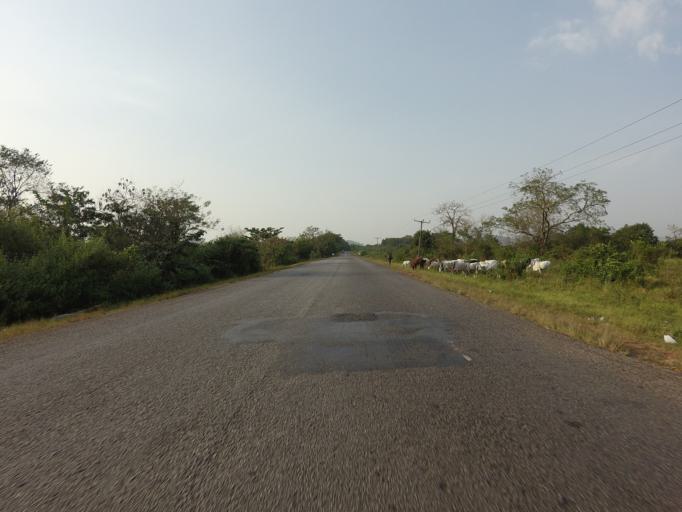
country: GH
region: Volta
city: Ho
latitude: 6.3935
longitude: 0.1812
